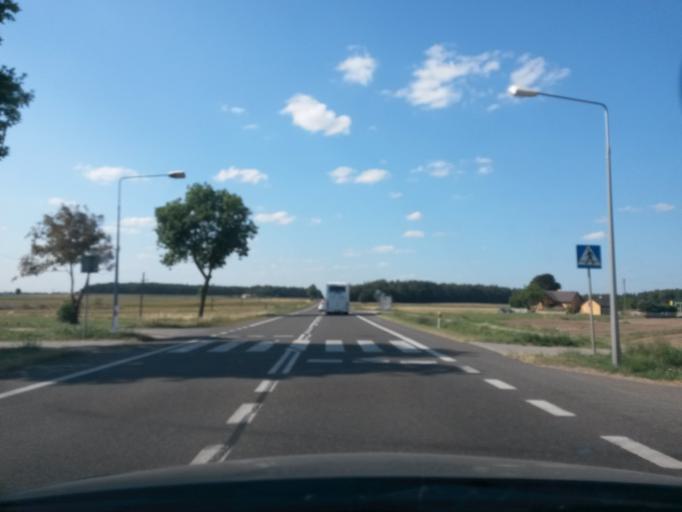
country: PL
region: Masovian Voivodeship
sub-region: Powiat plocki
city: Starozreby
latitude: 52.6560
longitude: 20.0830
